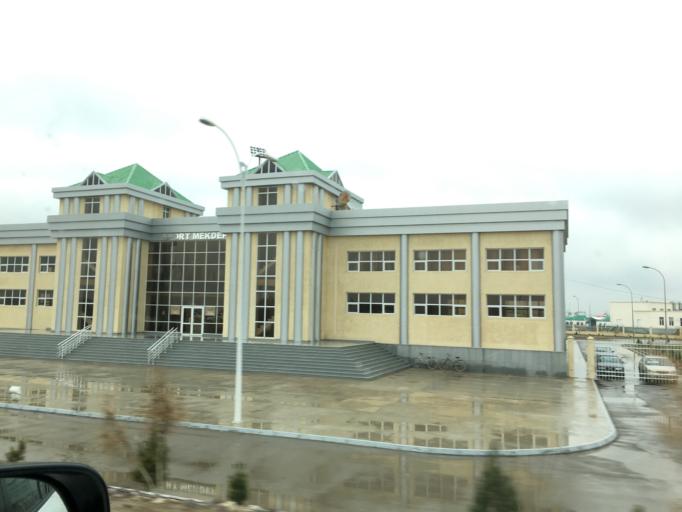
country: TM
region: Mary
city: Yoloeten
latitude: 37.2907
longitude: 62.3426
